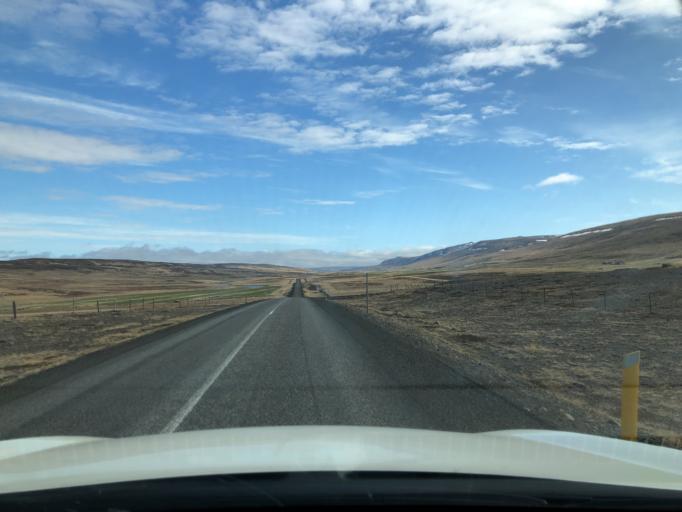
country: IS
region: West
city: Borgarnes
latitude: 65.1144
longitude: -21.6827
